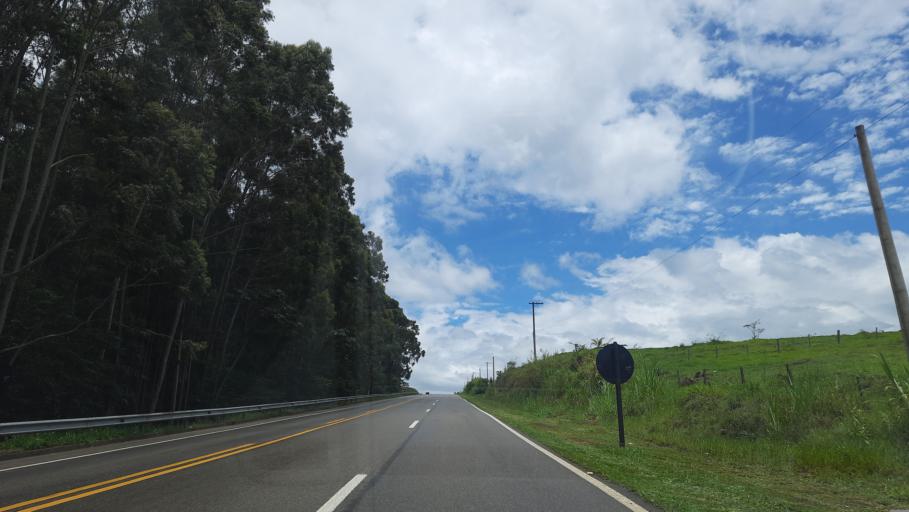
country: BR
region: Sao Paulo
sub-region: Vargem Grande Do Sul
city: Vargem Grande do Sul
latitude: -21.8013
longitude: -46.8020
